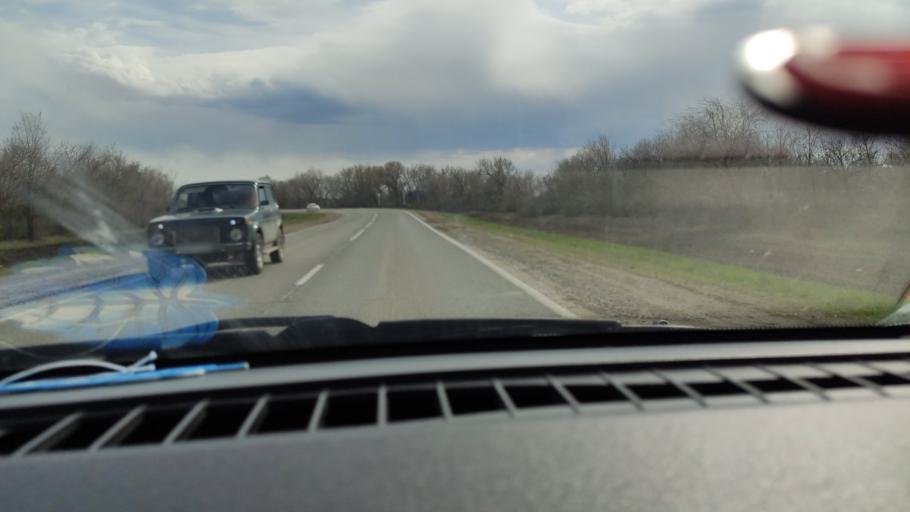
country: RU
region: Saratov
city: Privolzhskiy
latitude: 51.3519
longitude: 46.0447
